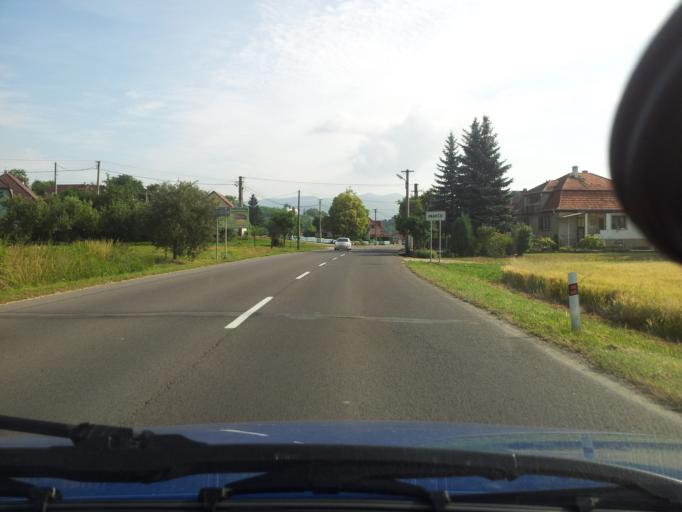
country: SK
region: Nitriansky
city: Partizanske
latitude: 48.6775
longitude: 18.3696
